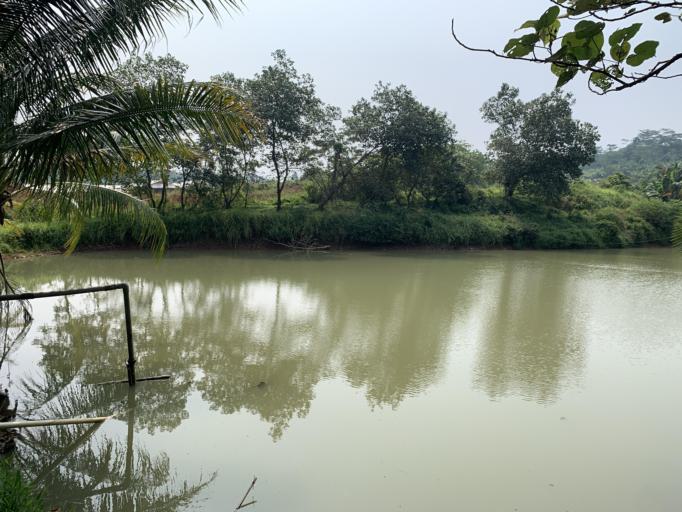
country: ID
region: West Java
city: Serpong
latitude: -6.3885
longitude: 106.5774
